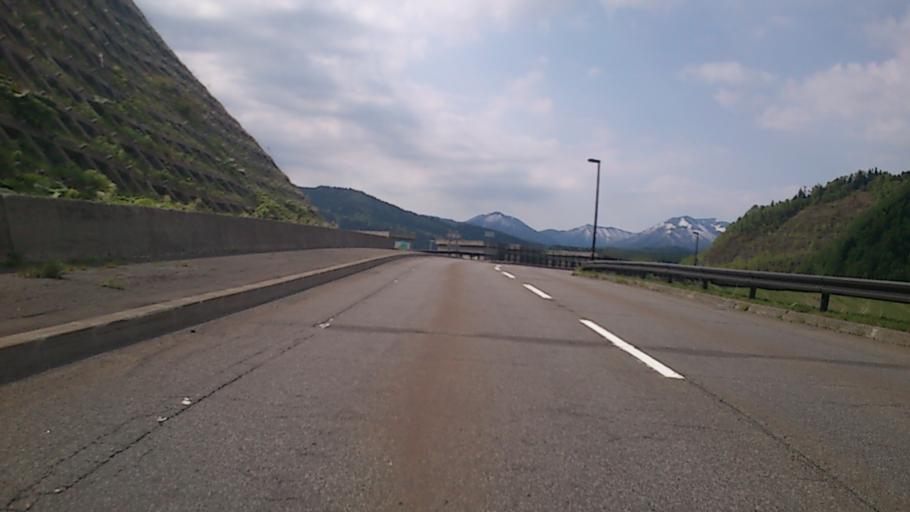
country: JP
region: Hokkaido
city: Kamikawa
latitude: 43.6790
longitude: 143.0374
